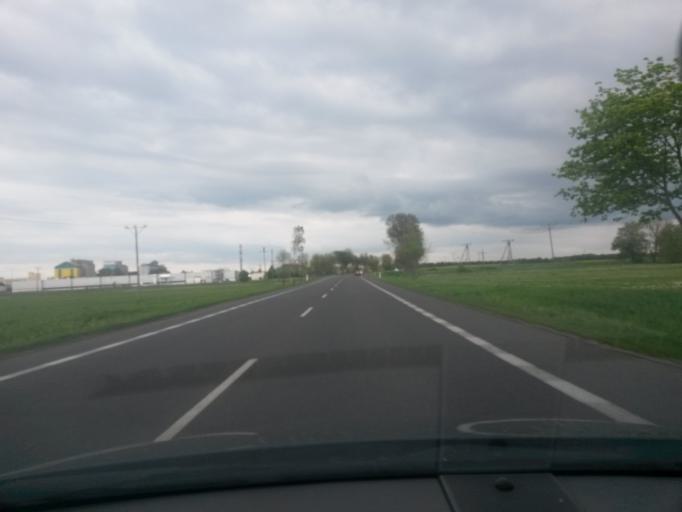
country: PL
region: Masovian Voivodeship
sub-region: Powiat plonski
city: Plonsk
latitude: 52.6158
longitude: 20.3421
